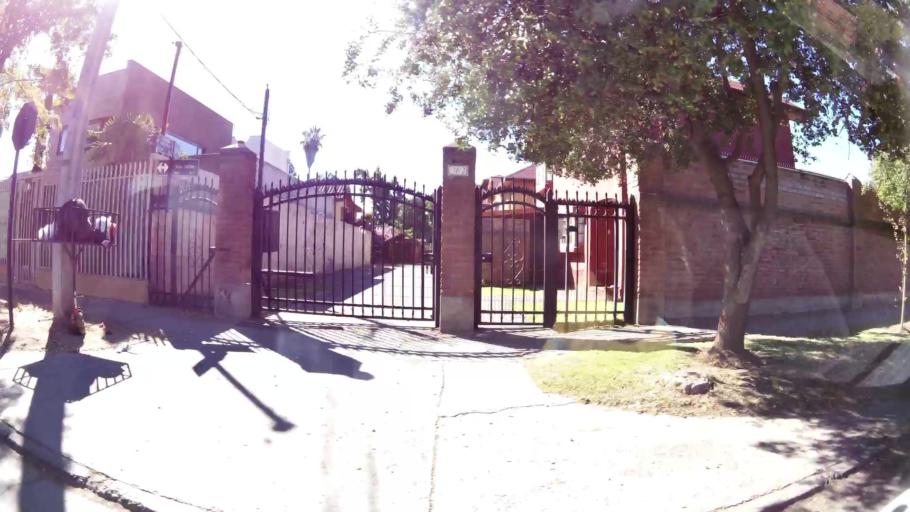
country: CL
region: O'Higgins
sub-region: Provincia de Cachapoal
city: Rancagua
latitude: -34.1801
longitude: -70.7144
